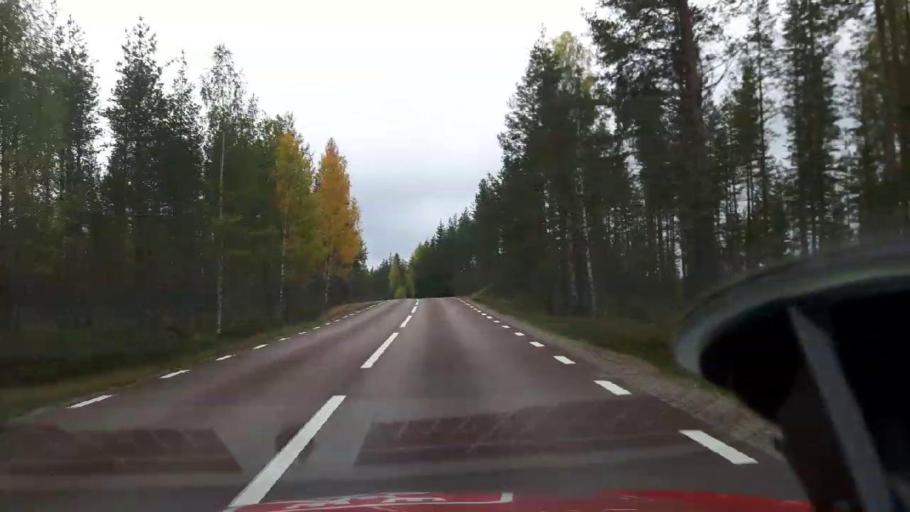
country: SE
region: Jaemtland
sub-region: Harjedalens Kommun
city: Sveg
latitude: 62.2110
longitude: 14.8445
